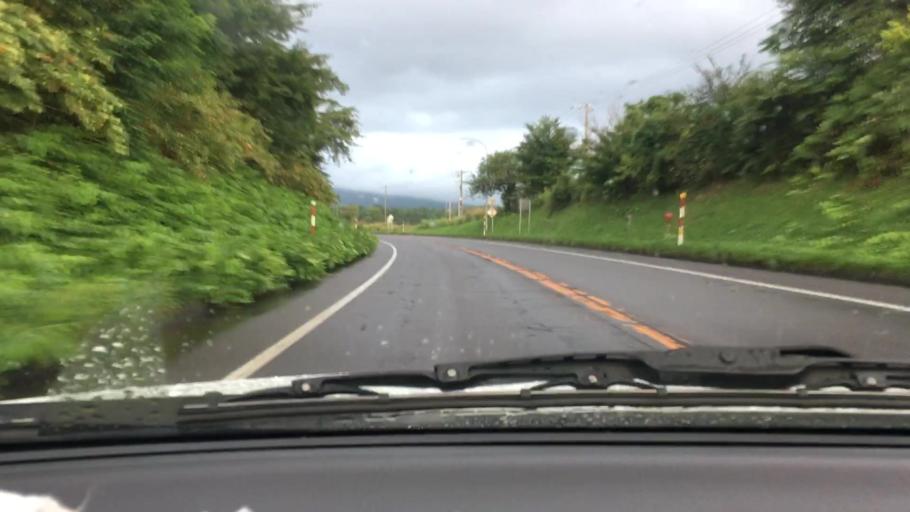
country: JP
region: Hokkaido
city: Nanae
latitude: 42.0814
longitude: 140.5892
